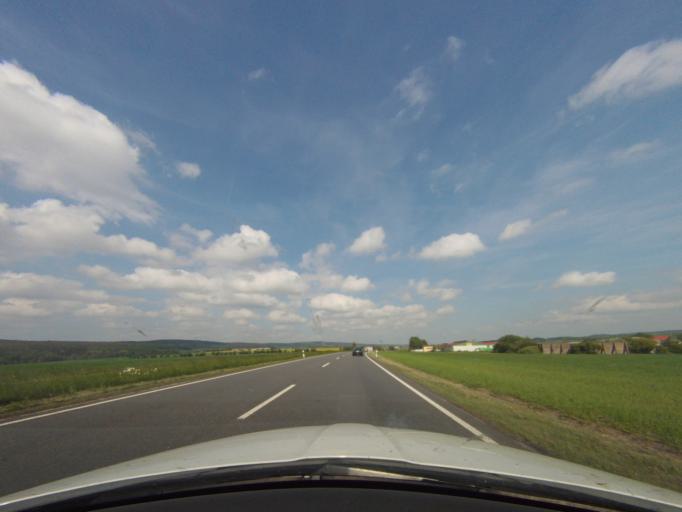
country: DE
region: Thuringia
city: Weira
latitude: 50.7296
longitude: 11.7062
